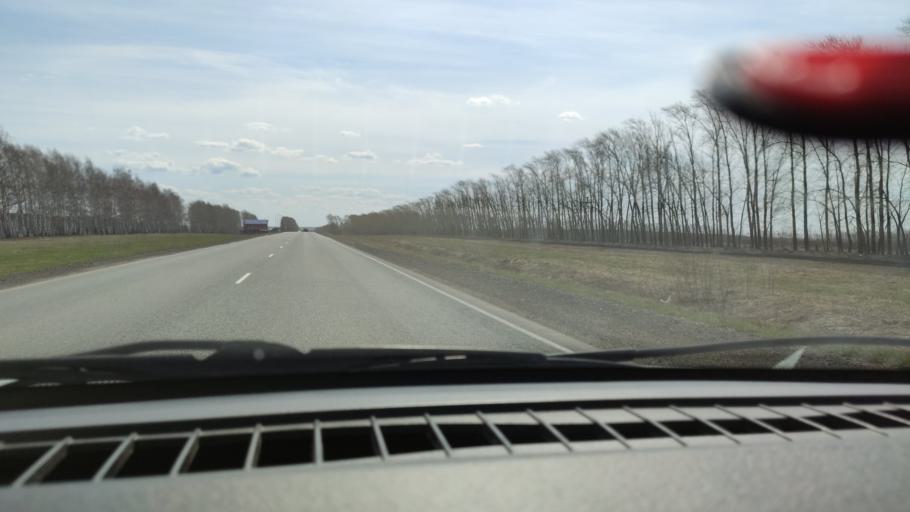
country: RU
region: Bashkortostan
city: Kushnarenkovo
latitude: 55.2260
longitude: 55.0881
